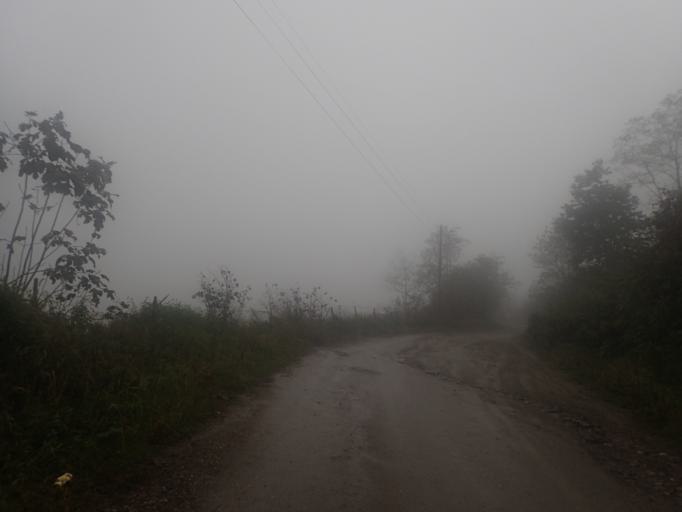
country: TR
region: Ordu
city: Persembe
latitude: 41.0242
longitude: 37.7124
